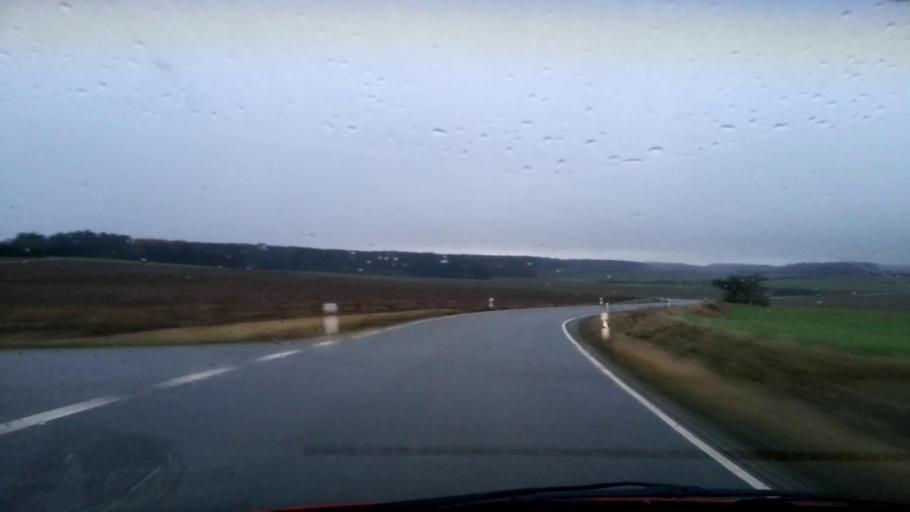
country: DE
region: Bavaria
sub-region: Upper Franconia
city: Konigsfeld
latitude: 49.9498
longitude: 11.1534
